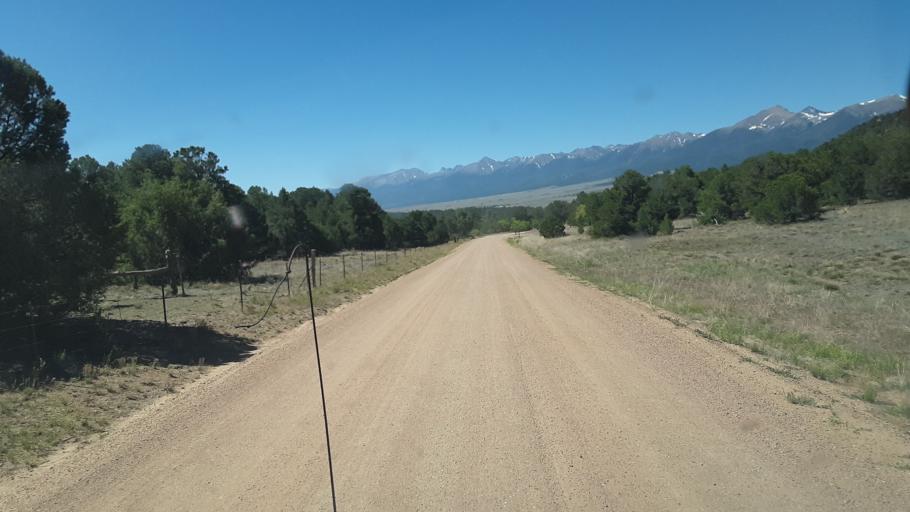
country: US
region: Colorado
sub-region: Custer County
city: Westcliffe
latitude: 38.2648
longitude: -105.5467
